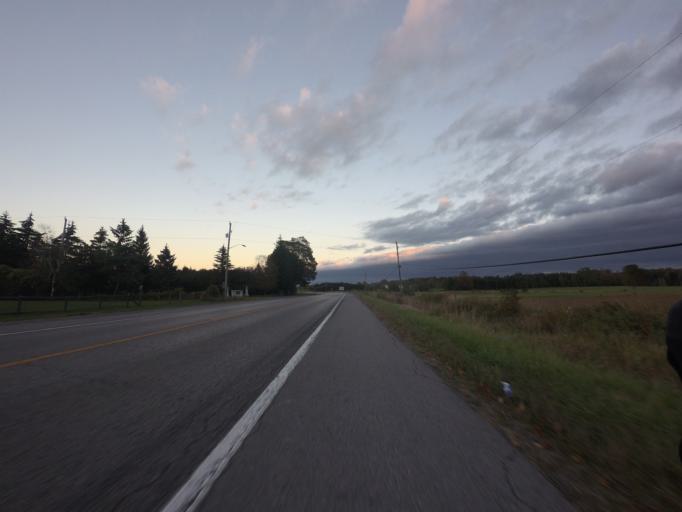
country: CA
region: Ontario
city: Quinte West
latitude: 44.0373
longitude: -77.6975
